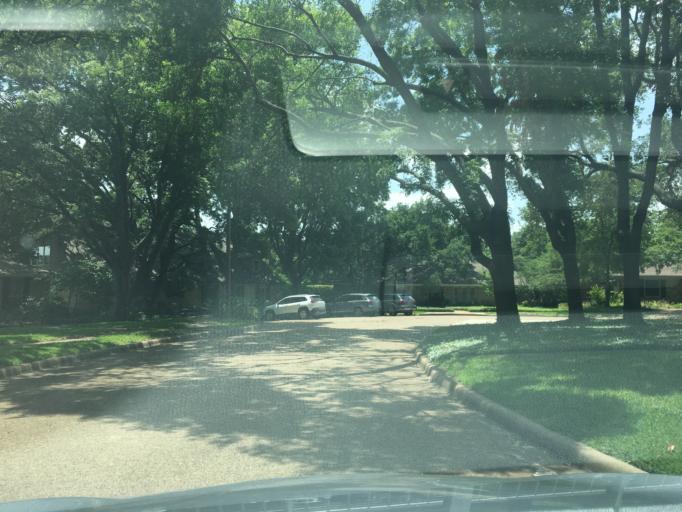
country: US
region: Texas
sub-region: Dallas County
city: University Park
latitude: 32.8848
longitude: -96.7757
